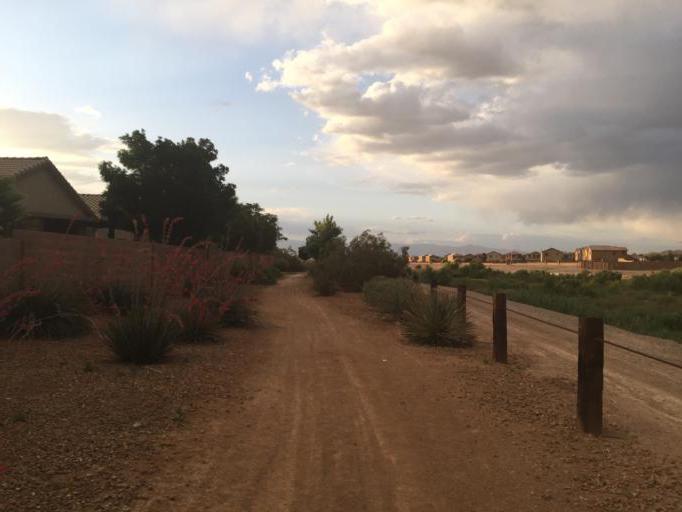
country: US
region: Nevada
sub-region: Clark County
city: Whitney
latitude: 36.1207
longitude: -115.0306
